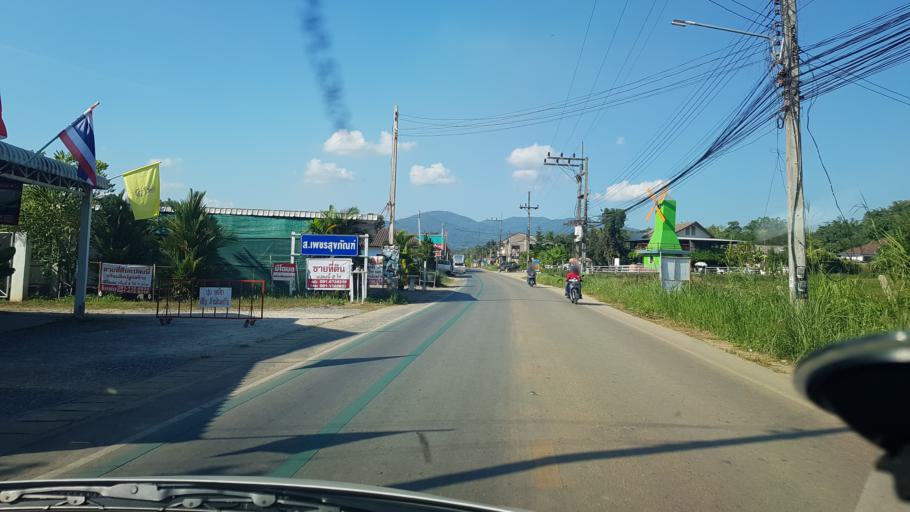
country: TH
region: Chiang Rai
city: Chiang Rai
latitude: 19.9471
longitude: 99.8103
